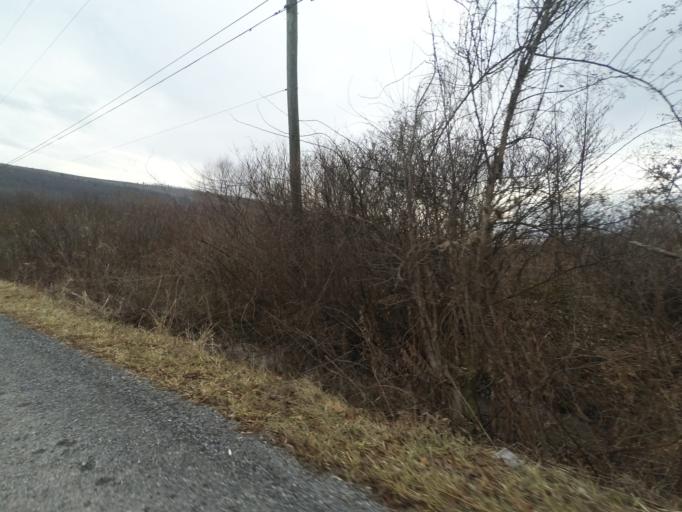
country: US
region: Pennsylvania
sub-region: Centre County
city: Stormstown
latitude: 40.8448
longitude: -77.9841
